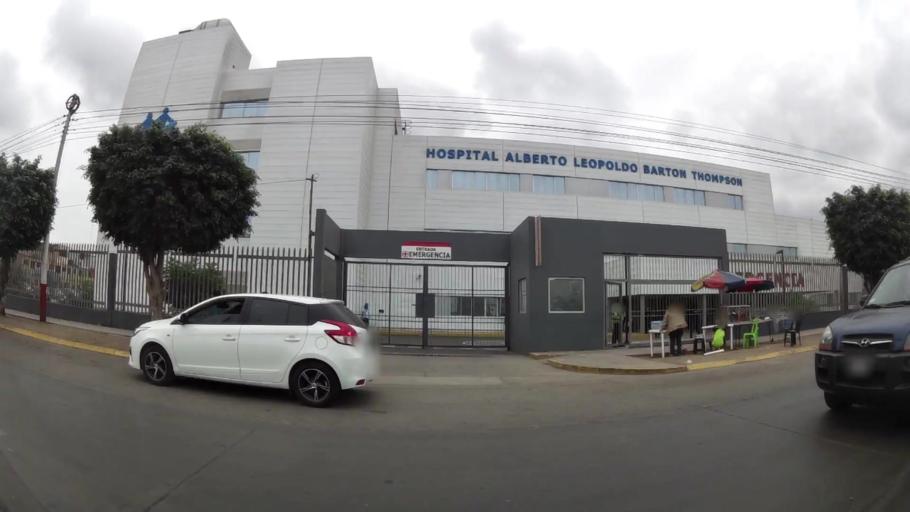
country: PE
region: Callao
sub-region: Callao
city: Callao
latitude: -12.0492
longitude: -77.1077
